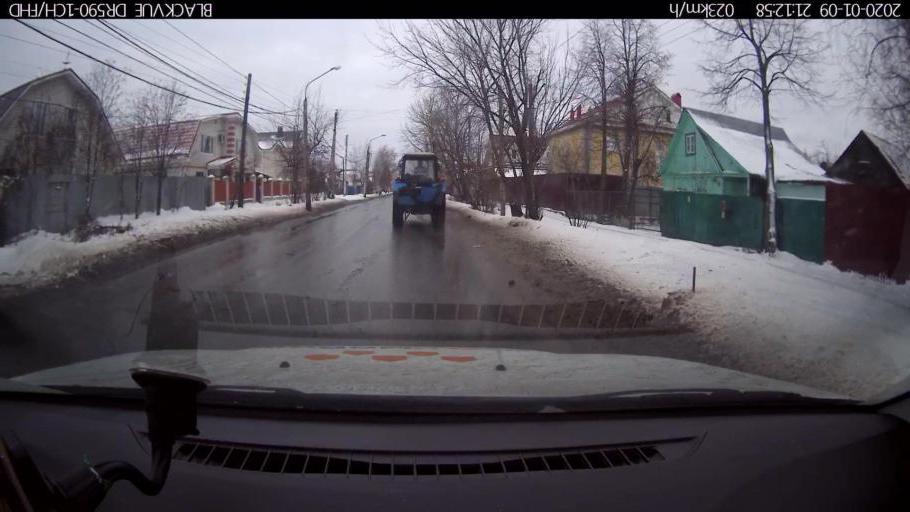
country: RU
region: Nizjnij Novgorod
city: Gorbatovka
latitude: 56.2959
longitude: 43.8501
